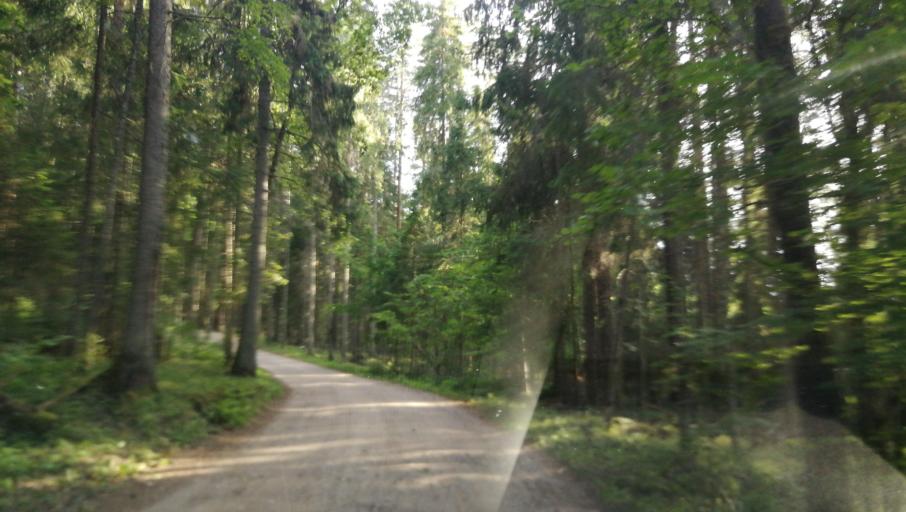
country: LV
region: Cesu Rajons
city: Cesis
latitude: 57.2887
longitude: 25.2126
